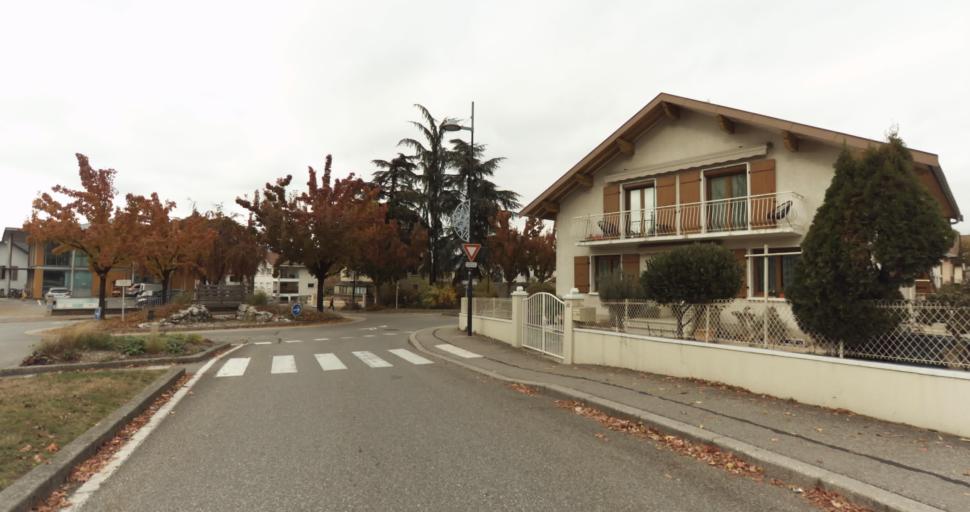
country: FR
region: Rhone-Alpes
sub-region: Departement de la Haute-Savoie
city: Annecy
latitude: 45.9082
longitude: 6.1107
